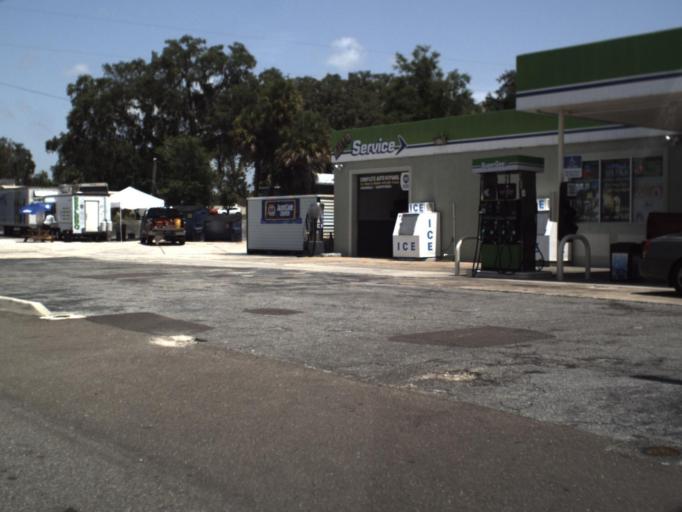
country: US
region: Florida
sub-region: Pinellas County
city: Palm Harbor
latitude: 28.0782
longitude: -82.7672
